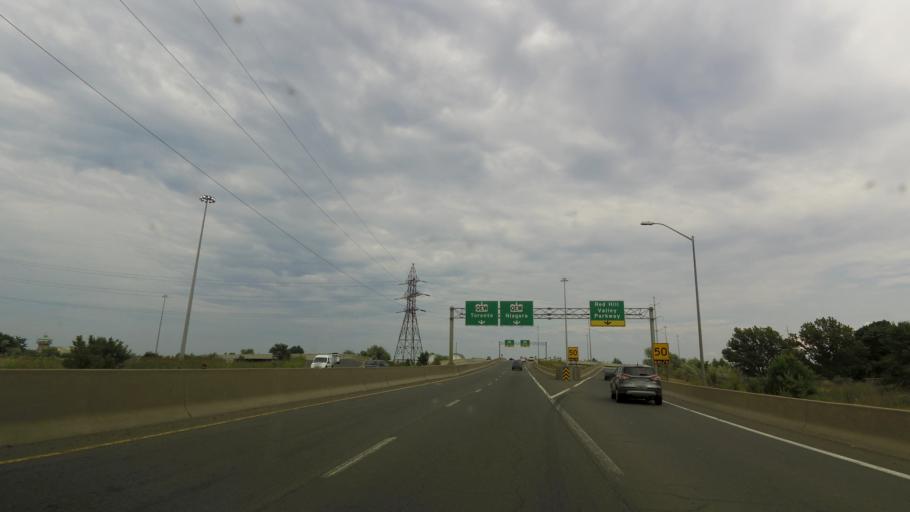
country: CA
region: Ontario
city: Hamilton
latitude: 43.2589
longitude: -79.7722
